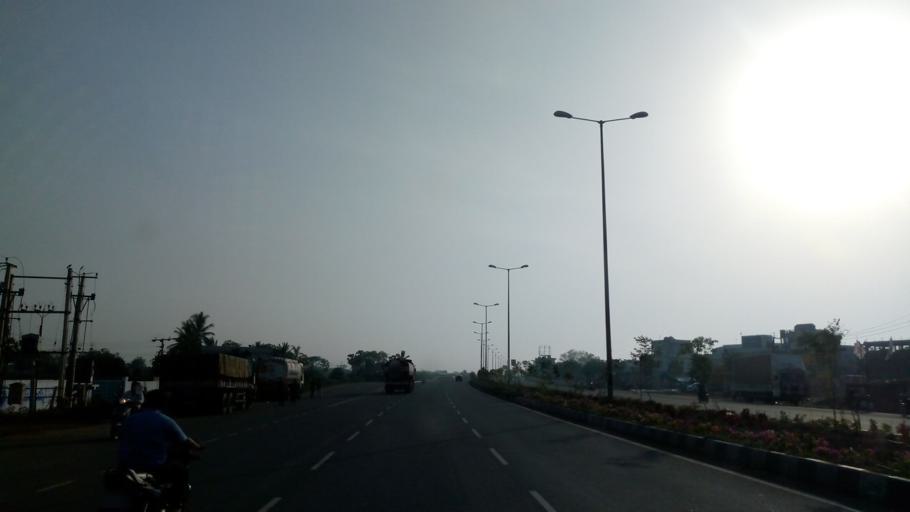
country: IN
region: Andhra Pradesh
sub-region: Guntur
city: Mangalagiri
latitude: 16.3885
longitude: 80.5363
